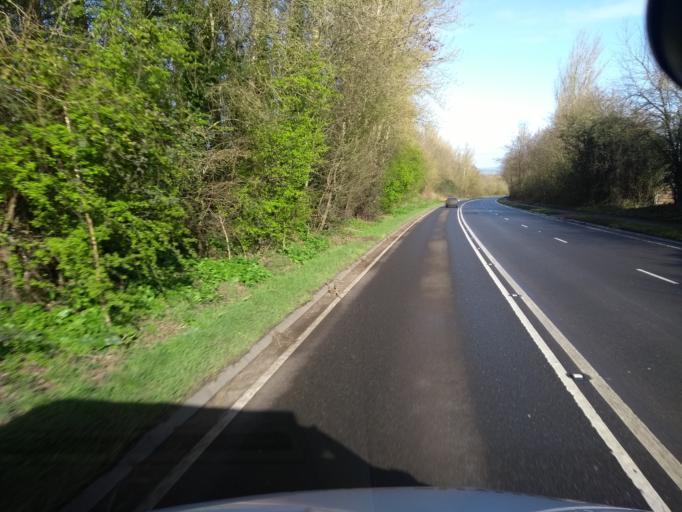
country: GB
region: England
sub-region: Somerset
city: Yeovil
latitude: 50.9588
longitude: -2.6509
